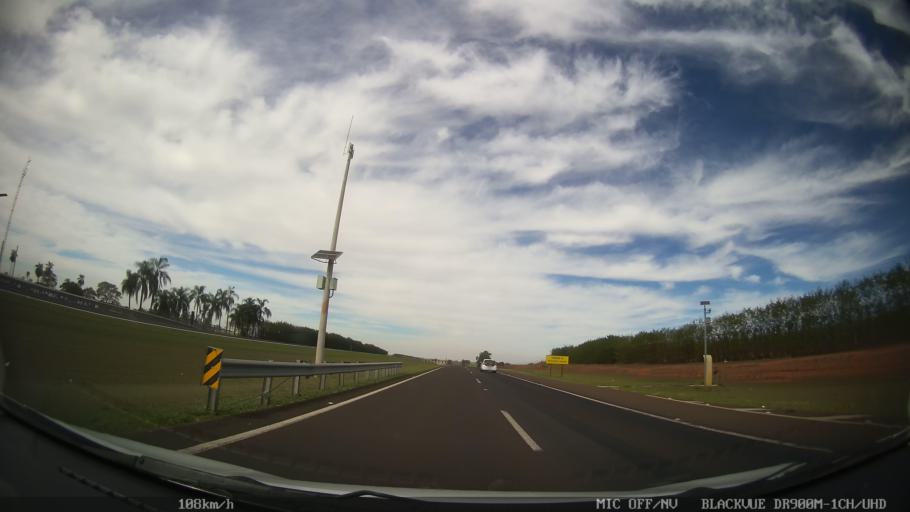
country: BR
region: Sao Paulo
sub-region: Taquaritinga
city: Taquaritinga
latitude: -21.5023
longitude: -48.5601
